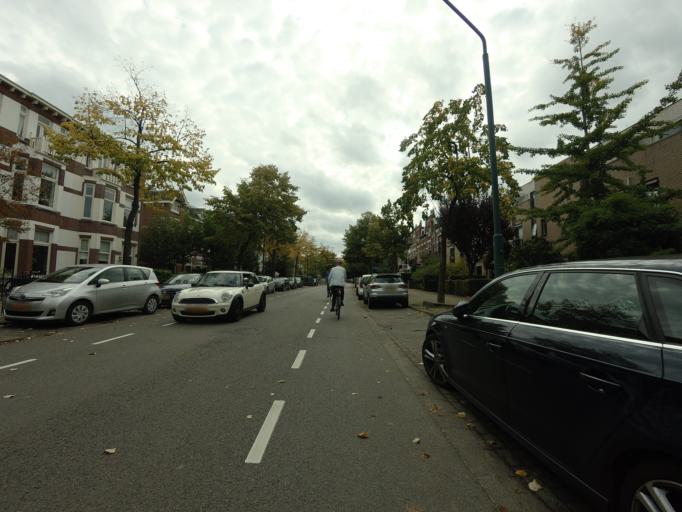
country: NL
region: North Brabant
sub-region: Gemeente Breda
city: Breda
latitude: 51.5712
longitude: 4.7773
